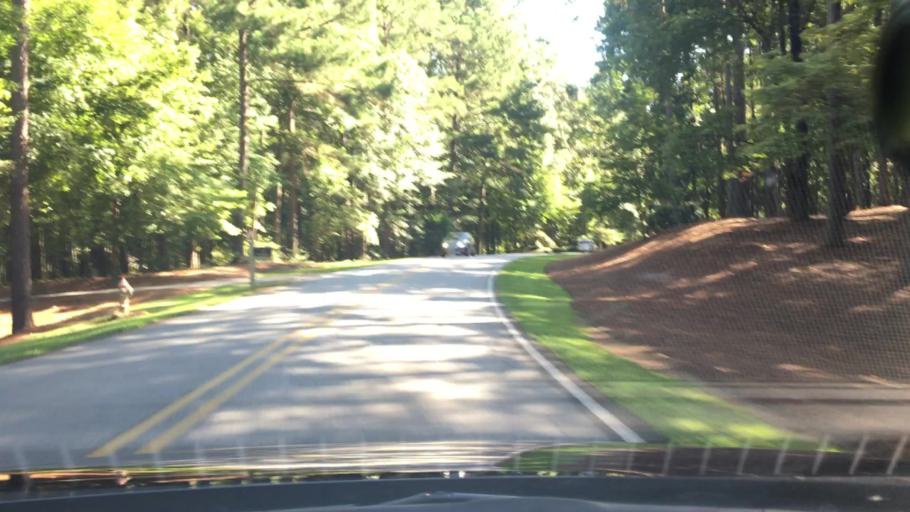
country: US
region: Georgia
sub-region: Putnam County
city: Jefferson
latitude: 33.3917
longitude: -83.2413
